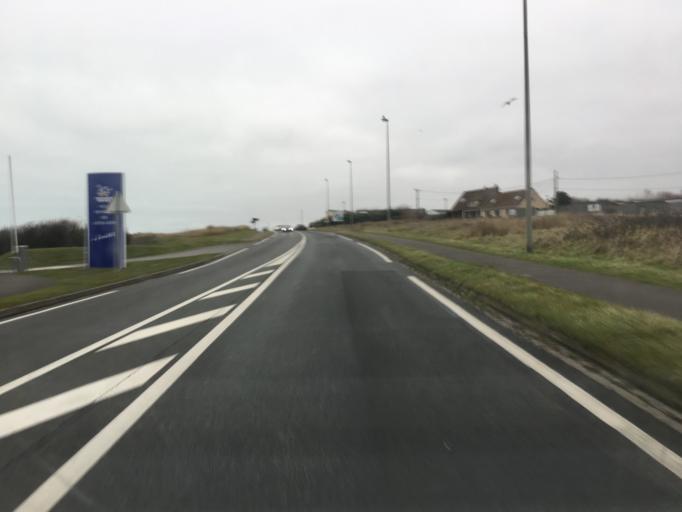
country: FR
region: Nord-Pas-de-Calais
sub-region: Departement du Pas-de-Calais
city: Saint-Martin-Boulogne
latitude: 50.7439
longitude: 1.5974
